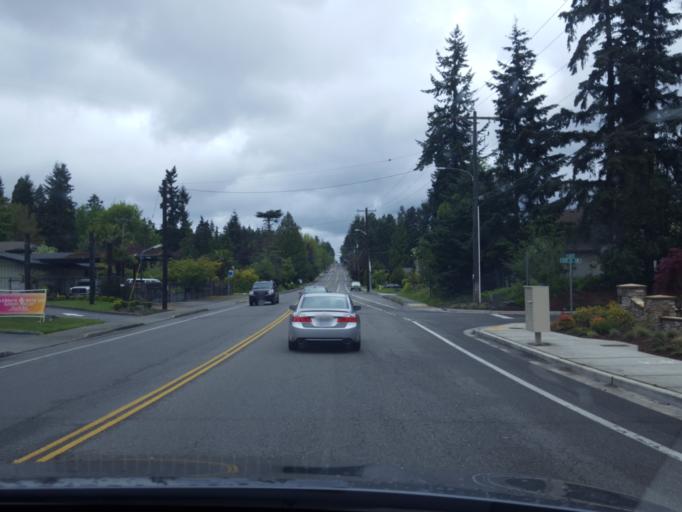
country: US
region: Washington
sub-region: Snohomish County
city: Esperance
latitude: 47.7788
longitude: -122.3353
